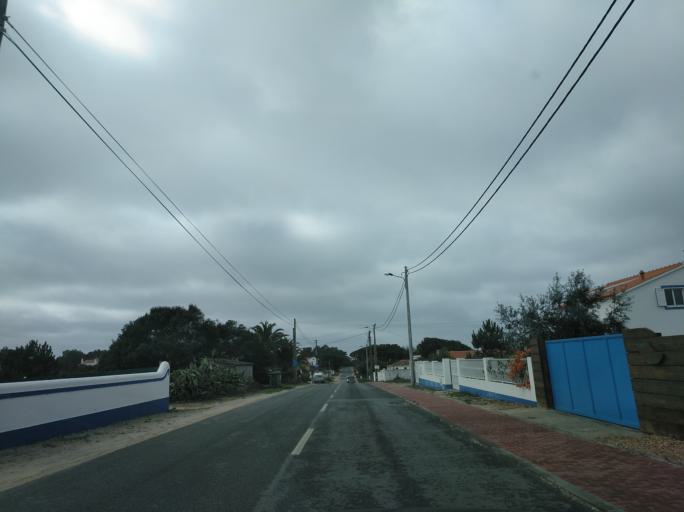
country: PT
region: Setubal
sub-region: Santiago do Cacem
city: Santo Andre
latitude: 38.1306
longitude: -8.7829
